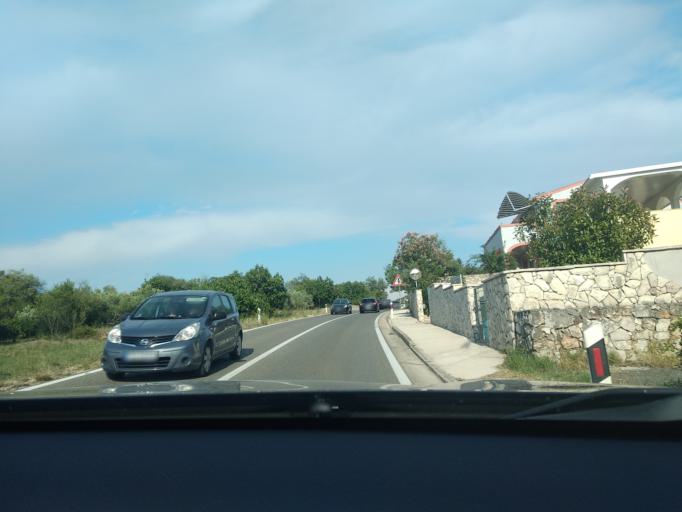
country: HR
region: Sibensko-Kniniska
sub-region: Grad Sibenik
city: Tisno
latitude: 43.8020
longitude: 15.6531
